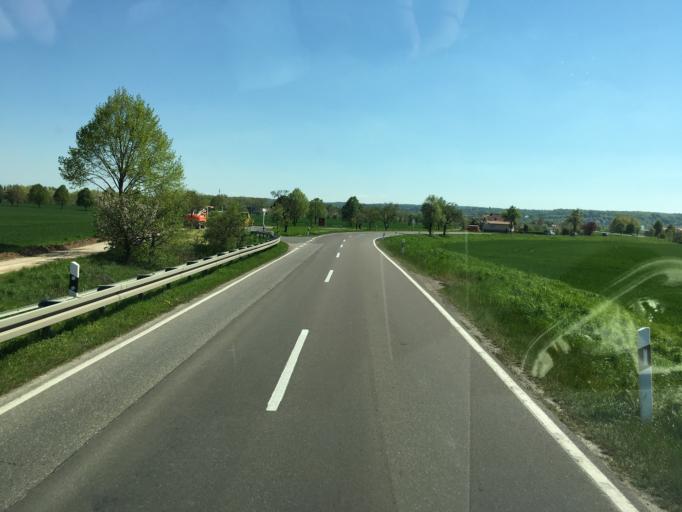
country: DE
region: Saxony-Anhalt
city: Naumburg
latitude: 51.1759
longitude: 11.7820
